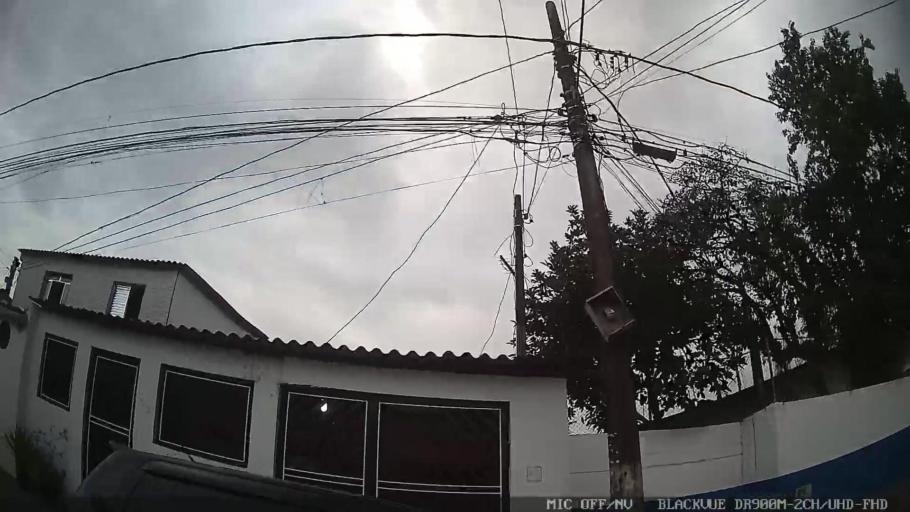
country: BR
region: Sao Paulo
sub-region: Santos
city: Santos
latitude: -23.9440
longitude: -46.2889
